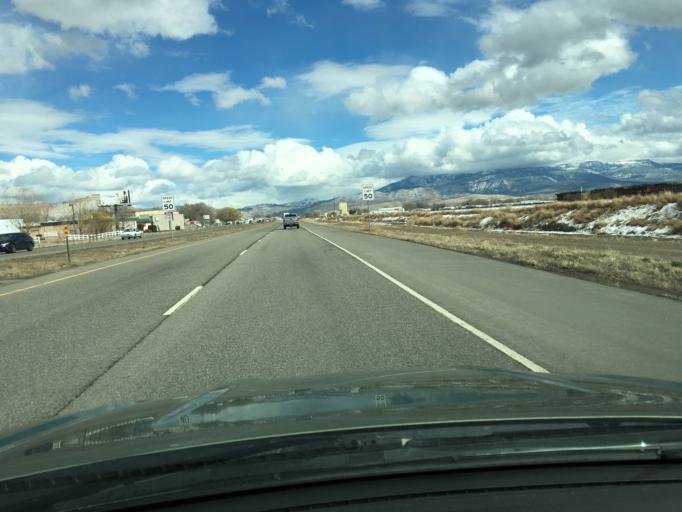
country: US
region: Colorado
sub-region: Mesa County
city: Fruitvale
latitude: 39.0740
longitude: -108.5098
